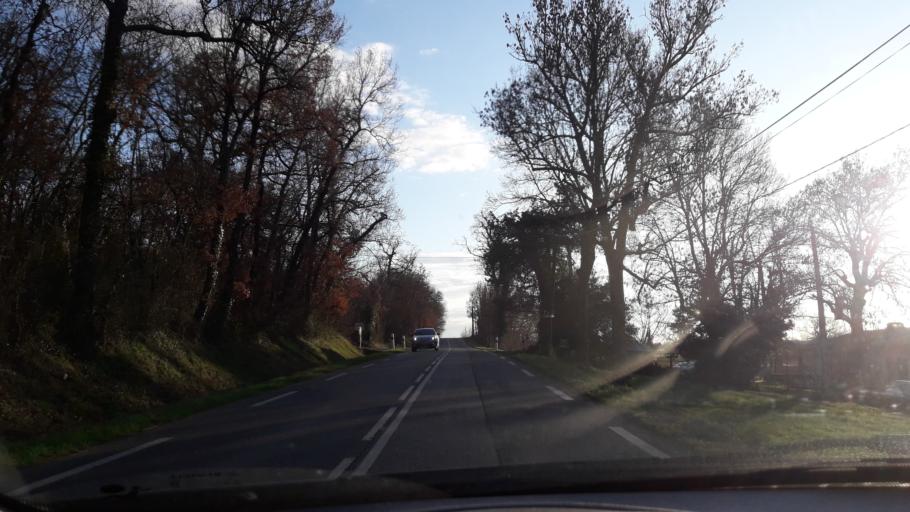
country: FR
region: Midi-Pyrenees
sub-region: Departement de la Haute-Garonne
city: Montaigut-sur-Save
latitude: 43.7101
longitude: 1.2459
